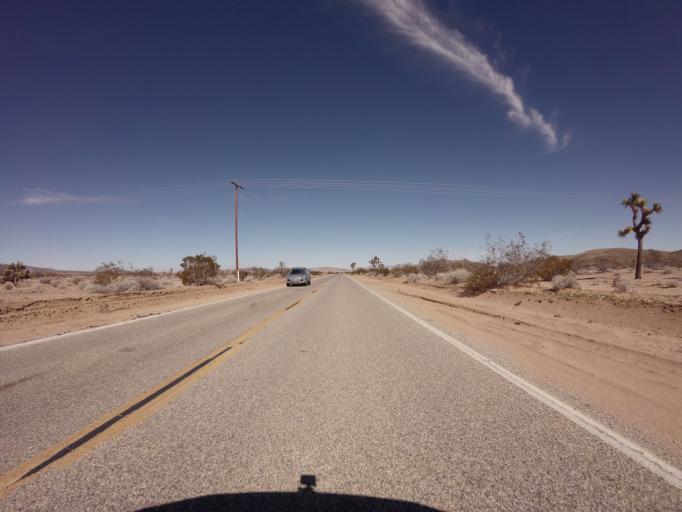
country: US
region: California
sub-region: San Bernardino County
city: Joshua Tree
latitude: 34.2440
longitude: -116.3933
